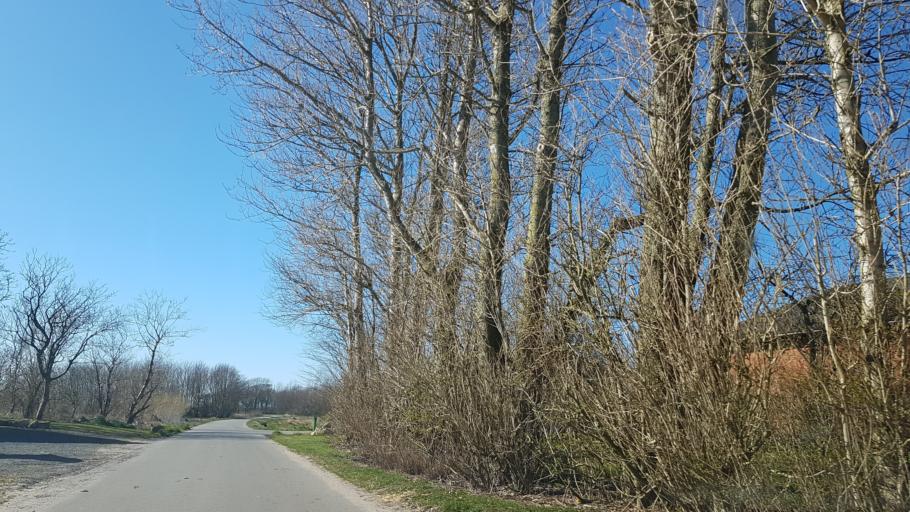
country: DK
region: South Denmark
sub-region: Esbjerg Kommune
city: Ribe
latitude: 55.2560
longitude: 8.6855
